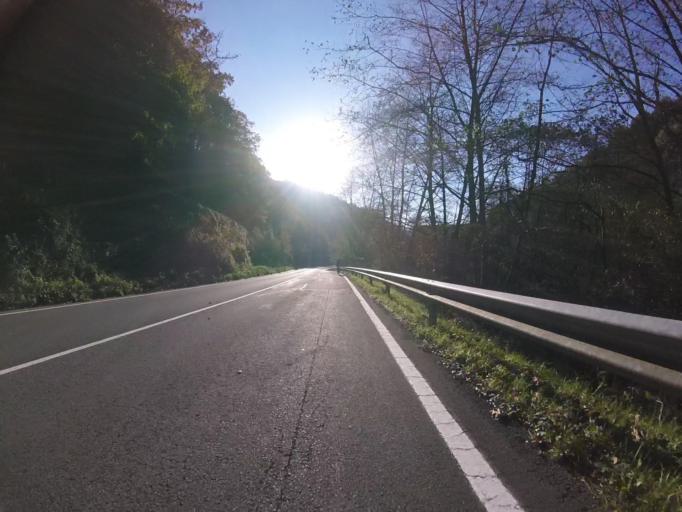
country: ES
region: Navarre
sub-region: Provincia de Navarra
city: Lesaka
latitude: 43.2494
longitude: -1.6715
